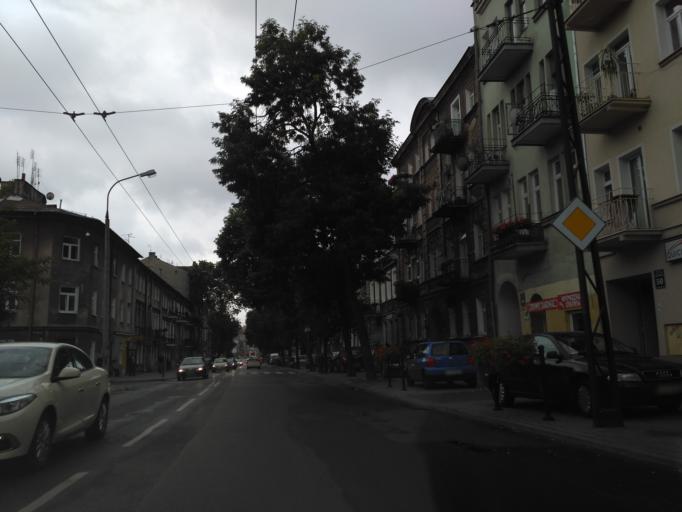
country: PL
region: Lublin Voivodeship
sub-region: Powiat lubelski
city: Lublin
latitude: 51.2554
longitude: 22.5702
